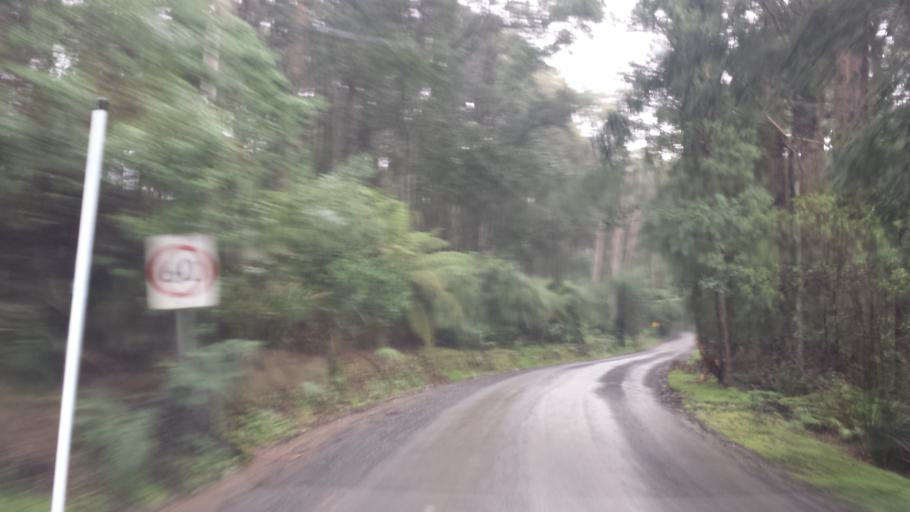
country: AU
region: Victoria
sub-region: Yarra Ranges
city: Monbulk
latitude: -37.8970
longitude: 145.4246
